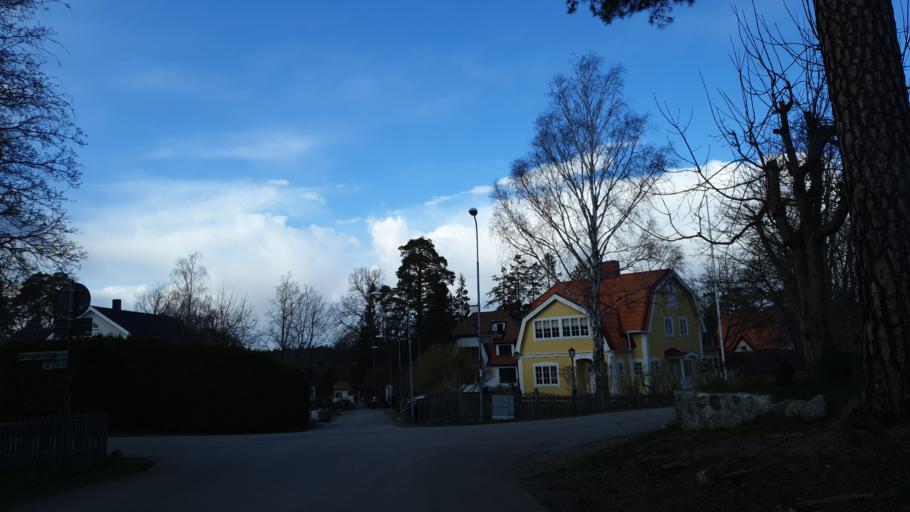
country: SE
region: Stockholm
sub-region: Lidingo
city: Lidingoe
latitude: 59.3687
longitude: 18.1410
